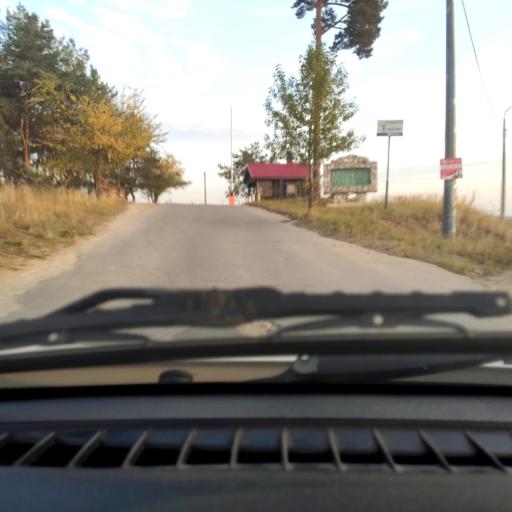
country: RU
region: Samara
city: Zhigulevsk
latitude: 53.4844
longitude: 49.5386
